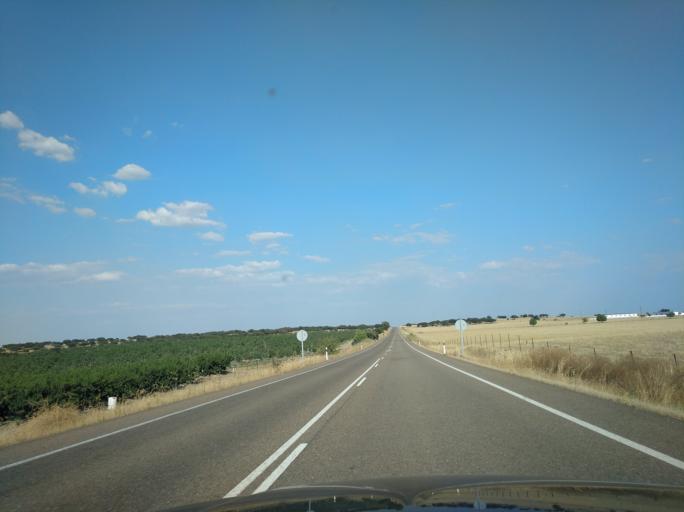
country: ES
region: Extremadura
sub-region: Provincia de Badajoz
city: Villanueva del Fresno
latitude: 38.3799
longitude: -7.2376
